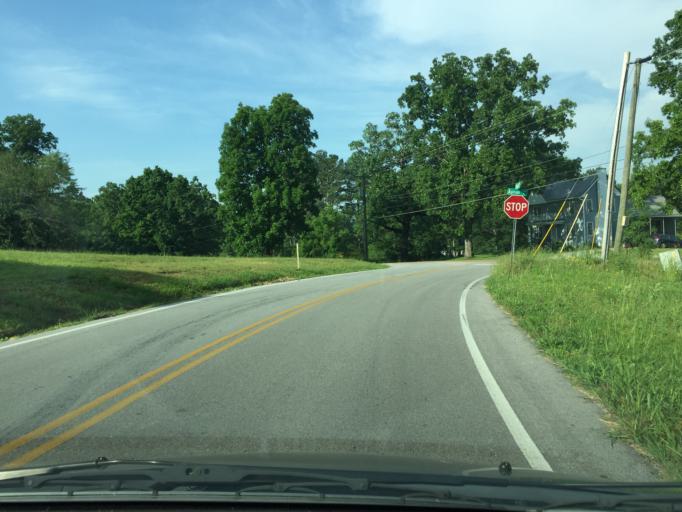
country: US
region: Tennessee
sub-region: Hamilton County
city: Apison
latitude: 35.0308
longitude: -85.0247
